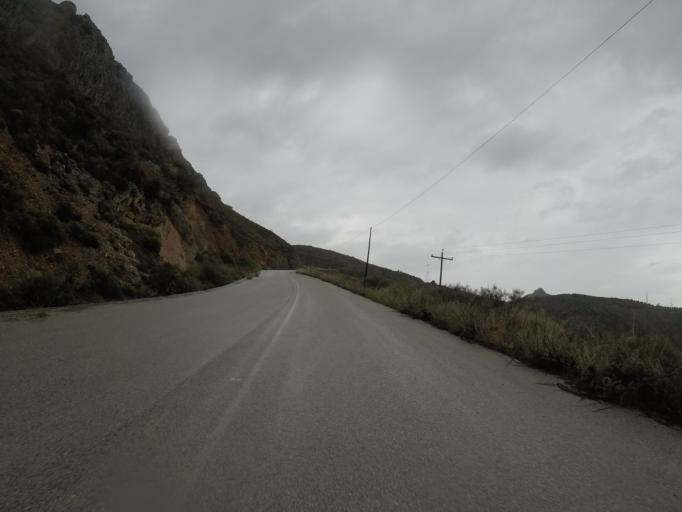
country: GR
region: Peloponnese
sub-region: Nomos Korinthias
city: Arkhaia Korinthos
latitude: 37.8947
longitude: 22.8683
